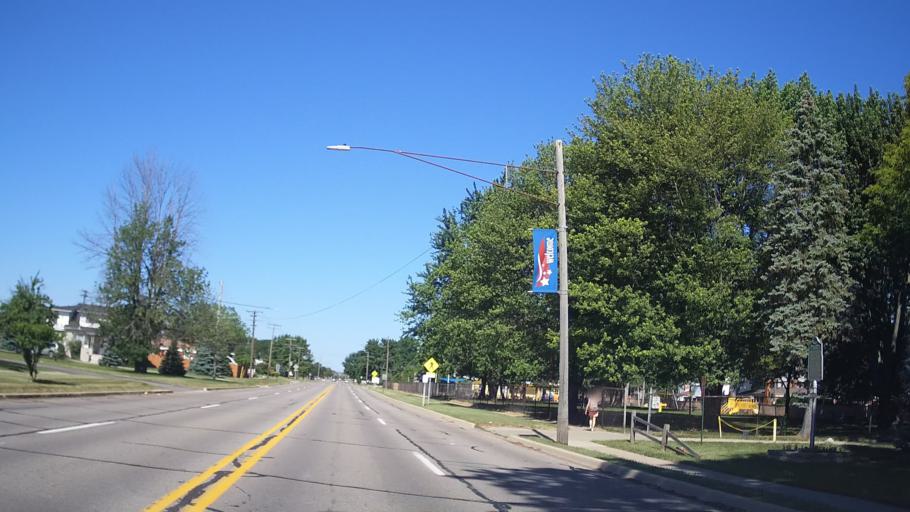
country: US
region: Michigan
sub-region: Macomb County
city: Fraser
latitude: 42.5319
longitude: -82.9299
